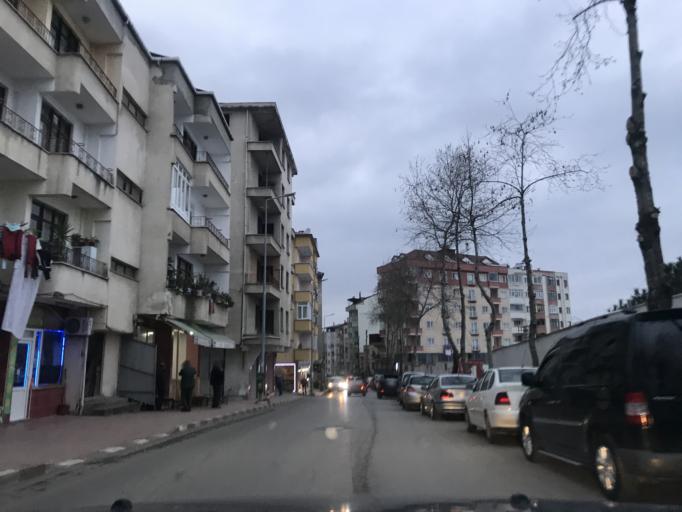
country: TR
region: Trabzon
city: Akcaabat
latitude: 41.0167
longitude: 39.5843
